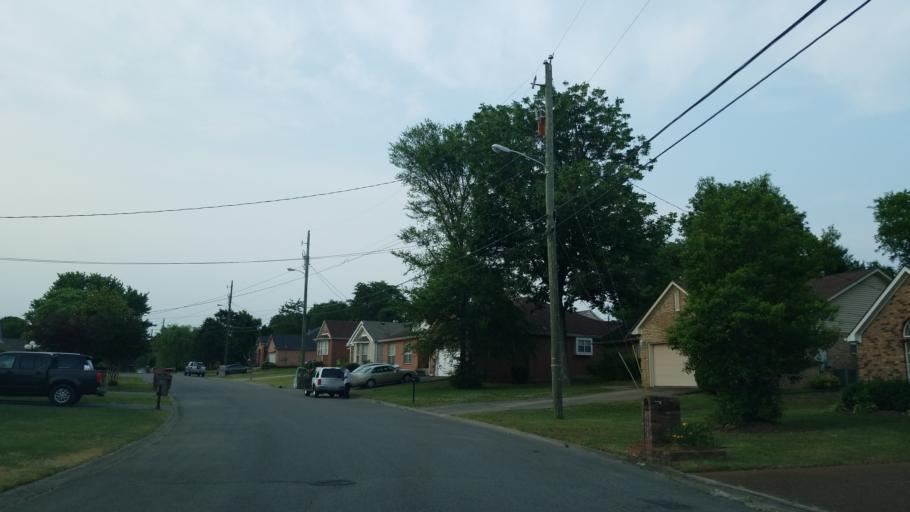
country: US
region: Tennessee
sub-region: Rutherford County
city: La Vergne
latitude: 36.0283
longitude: -86.5860
